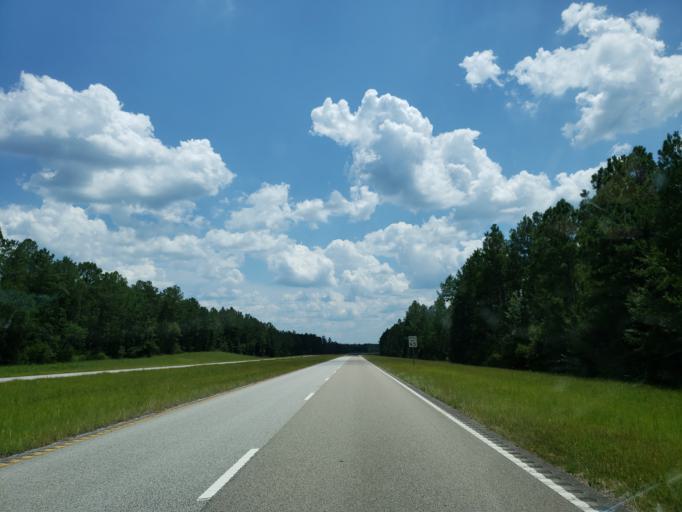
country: US
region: Mississippi
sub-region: Greene County
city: Leakesville
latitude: 31.1639
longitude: -88.5009
